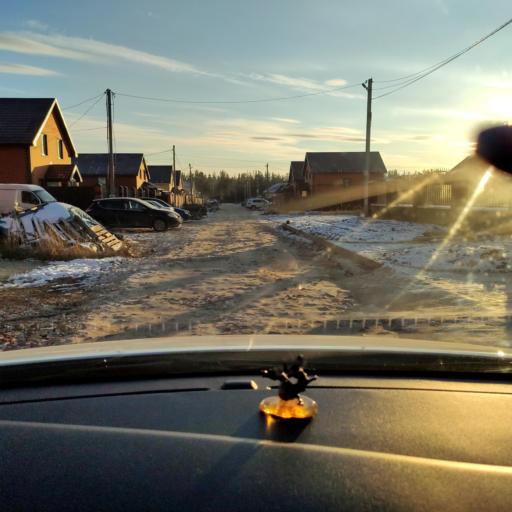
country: RU
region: Tatarstan
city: Stolbishchi
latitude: 55.6050
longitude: 49.1404
